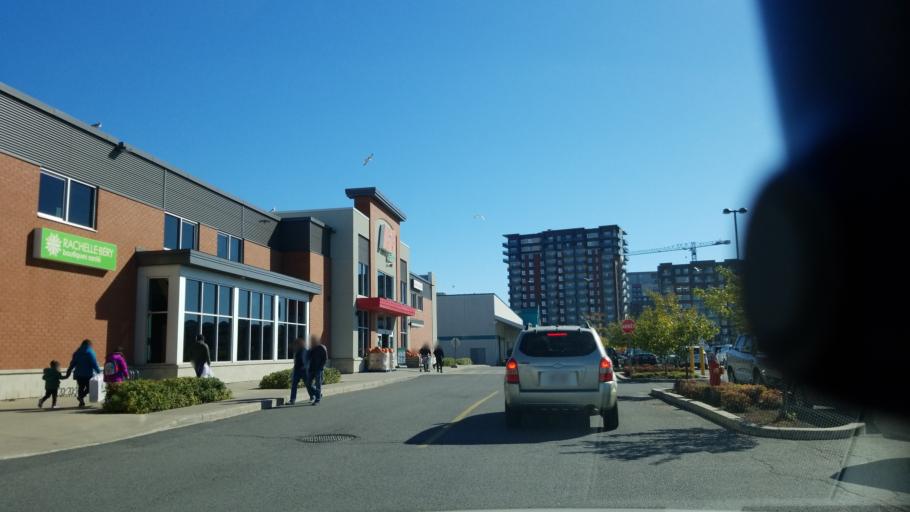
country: CA
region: Quebec
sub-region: Laval
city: Laval
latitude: 45.5628
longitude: -73.7274
